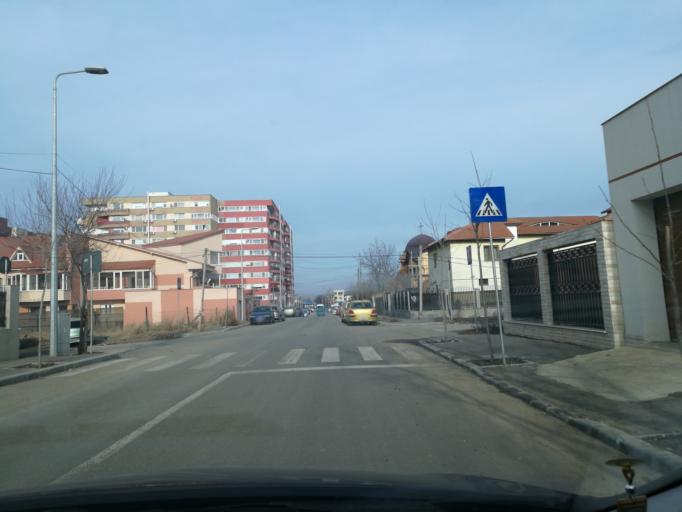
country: RO
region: Constanta
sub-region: Municipiul Constanta
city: Constanta
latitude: 44.1860
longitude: 28.6117
